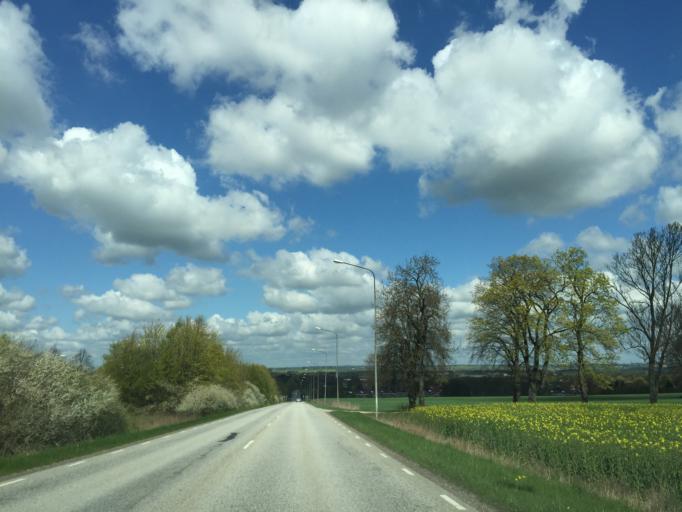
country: SE
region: Skane
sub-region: Lunds Kommun
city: Genarp
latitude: 55.7088
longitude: 13.3431
